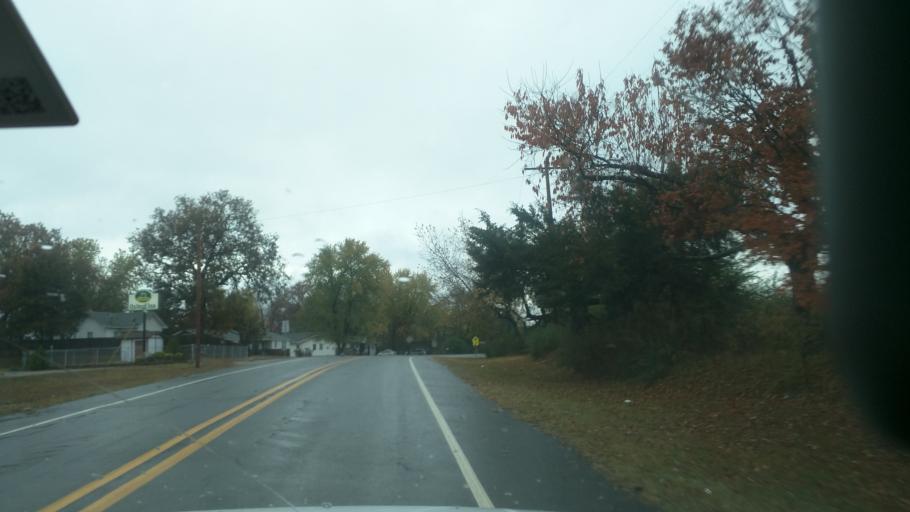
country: US
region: Arkansas
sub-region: Franklin County
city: Ozark
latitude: 35.4901
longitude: -93.8434
